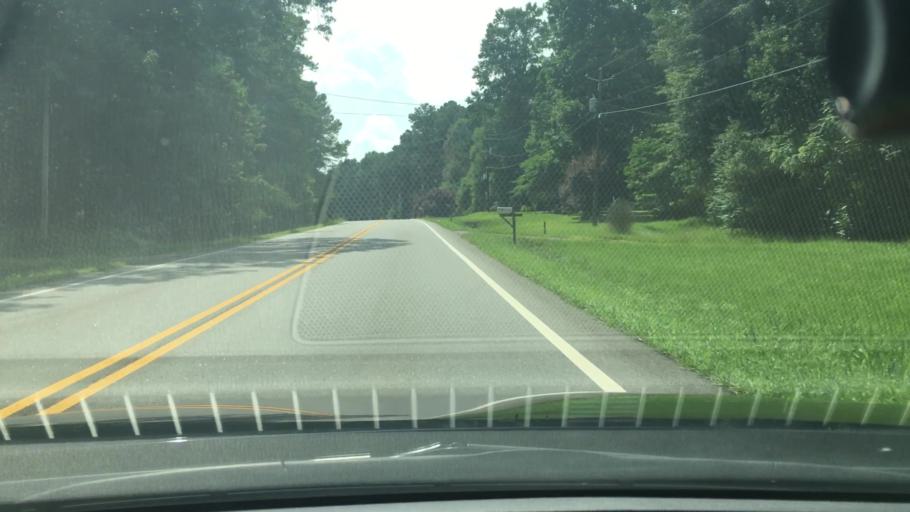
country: US
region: Georgia
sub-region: Coweta County
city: East Newnan
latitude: 33.3362
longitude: -84.7365
